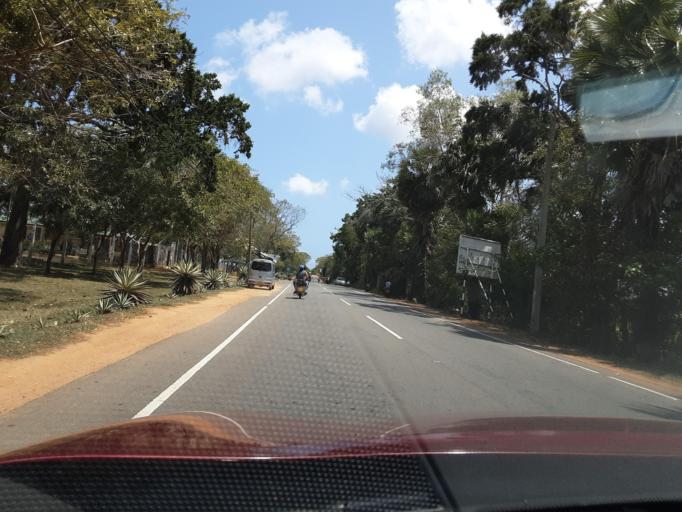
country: LK
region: Southern
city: Tangalla
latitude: 6.2543
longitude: 81.2273
